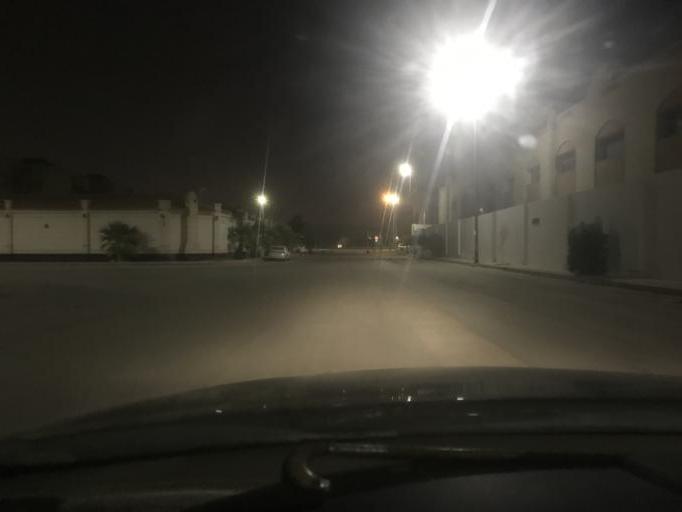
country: SA
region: Ar Riyad
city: Riyadh
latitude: 24.7351
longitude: 46.7814
